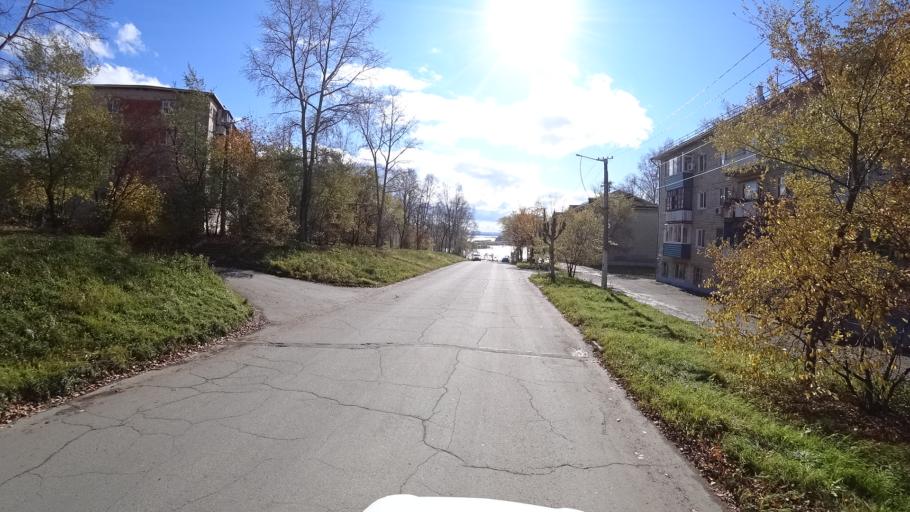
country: RU
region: Khabarovsk Krai
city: Amursk
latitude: 50.2165
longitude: 136.9032
